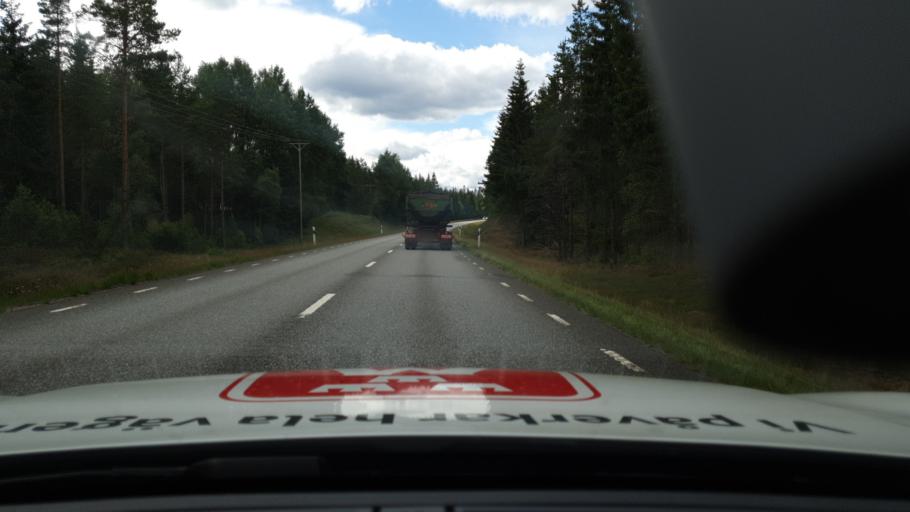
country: SE
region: Joenkoeping
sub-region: Jonkopings Kommun
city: Taberg
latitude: 57.6641
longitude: 13.8362
